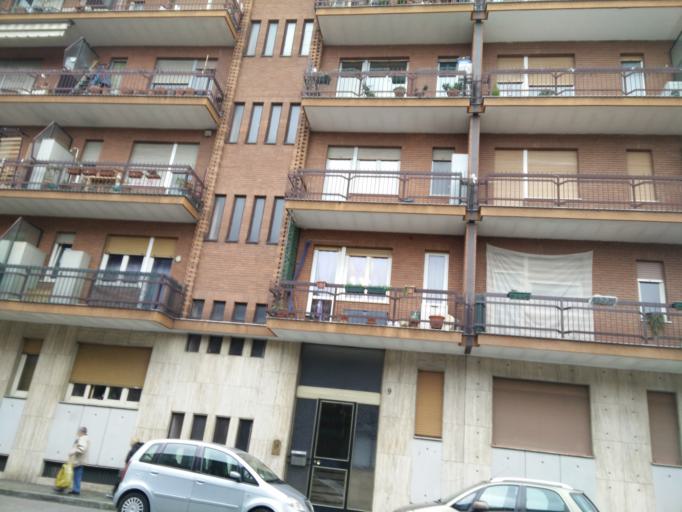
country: IT
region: Piedmont
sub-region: Provincia di Torino
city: Nichelino
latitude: 45.0048
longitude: 7.6473
